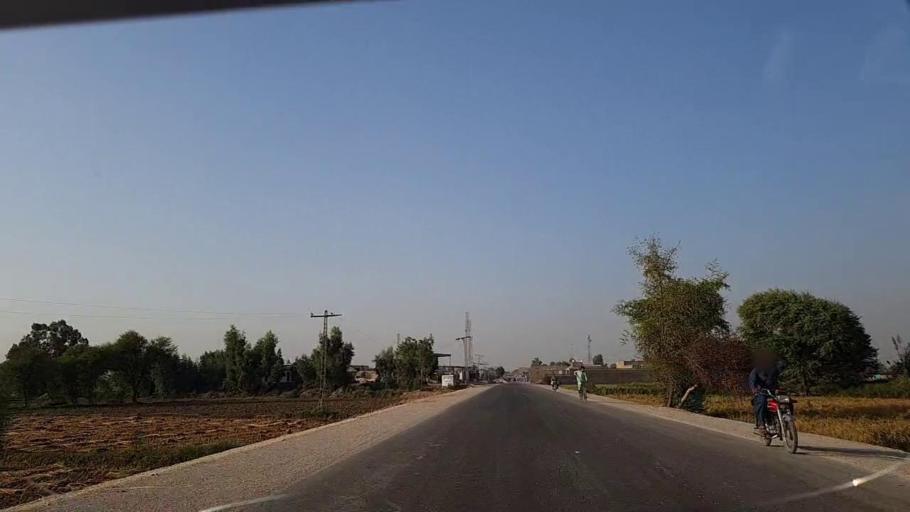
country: PK
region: Sindh
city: Rustam jo Goth
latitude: 27.9594
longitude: 68.8068
